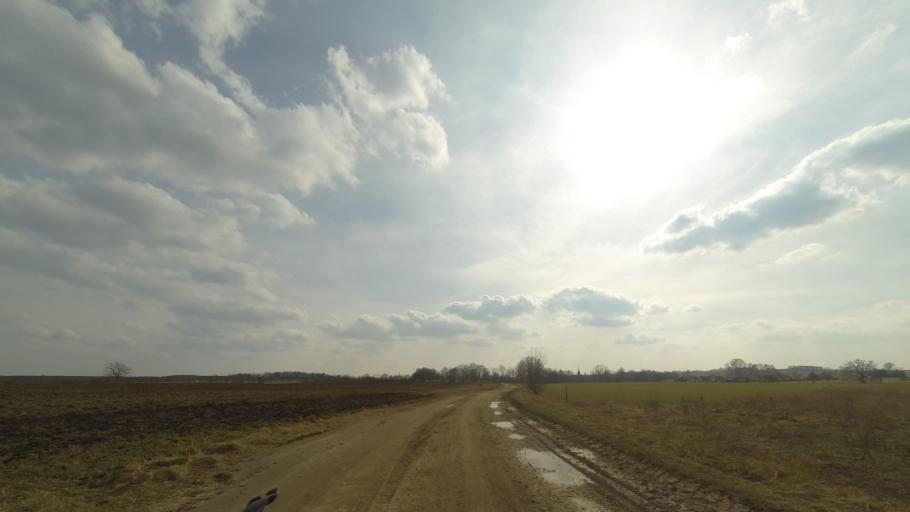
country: DE
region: Saxony
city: Radeburg
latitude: 51.2453
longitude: 13.7055
